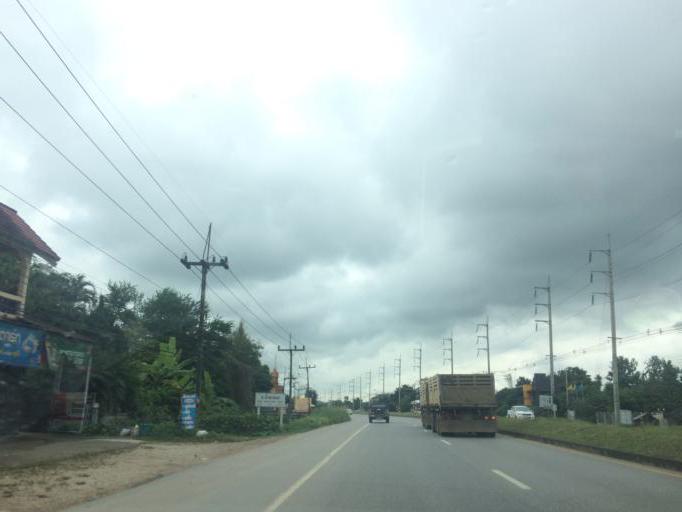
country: TH
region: Chiang Rai
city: Mae Chan
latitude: 20.0735
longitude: 99.8756
